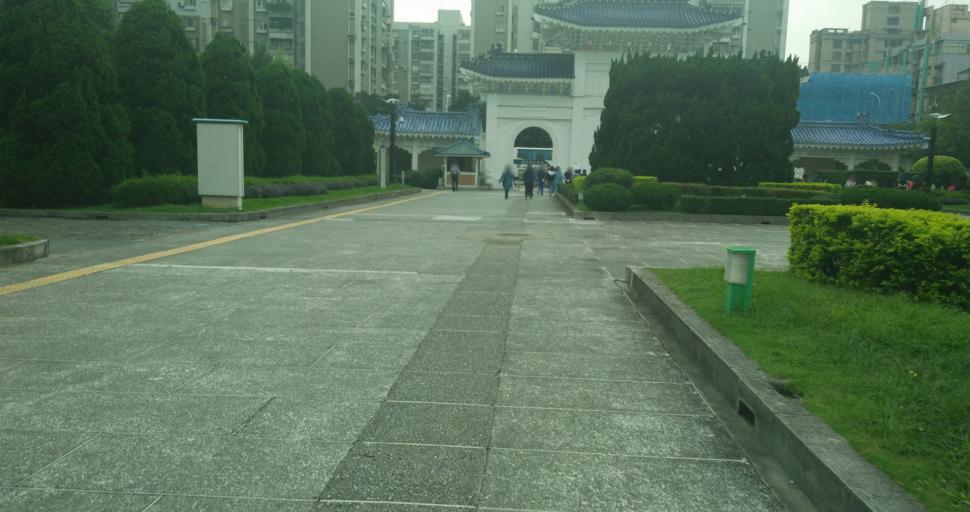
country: TW
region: Taipei
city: Taipei
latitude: 25.0337
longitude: 121.5214
